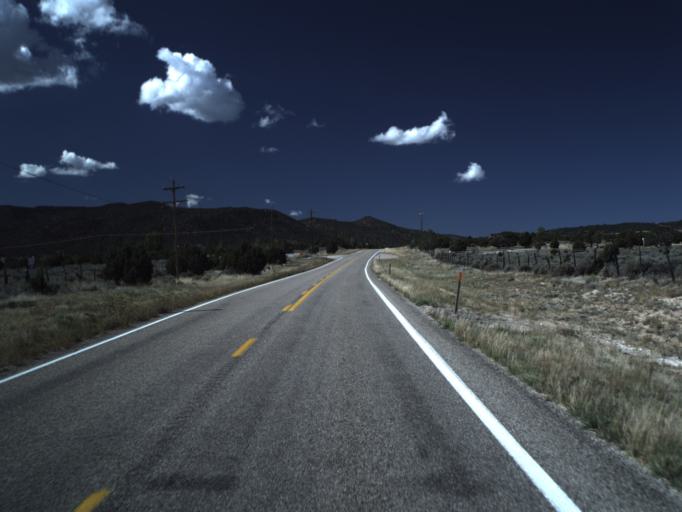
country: US
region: Utah
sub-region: Iron County
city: Cedar City
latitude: 37.6465
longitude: -113.2417
